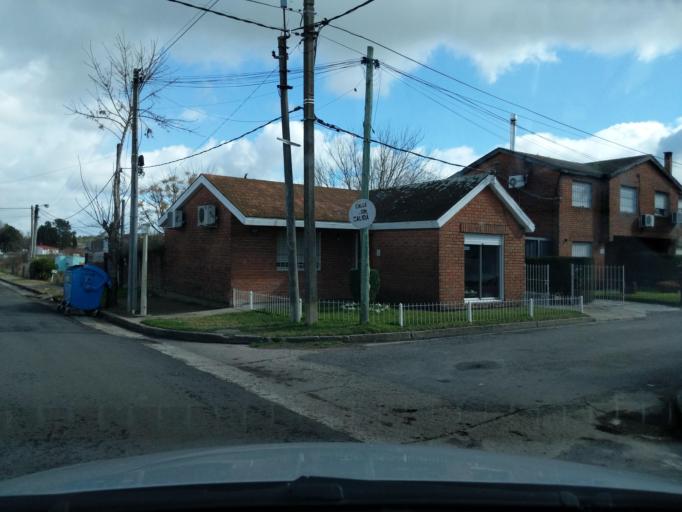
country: UY
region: Florida
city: Florida
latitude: -34.1024
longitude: -56.2216
